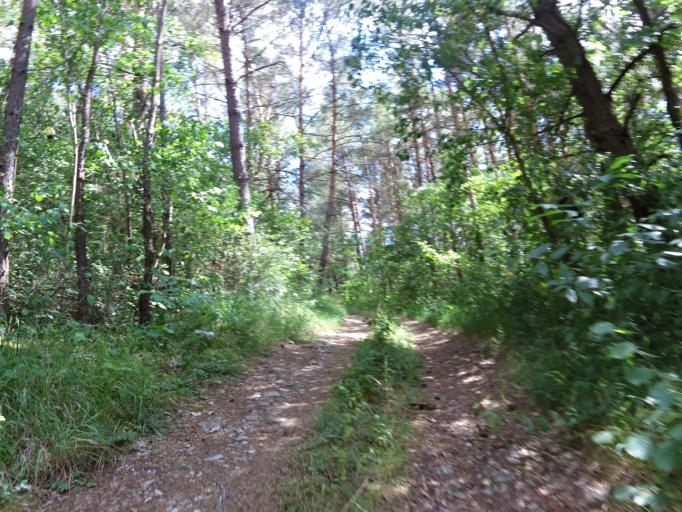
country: DE
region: Bavaria
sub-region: Regierungsbezirk Unterfranken
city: Gerbrunn
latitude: 49.7718
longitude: 9.9978
